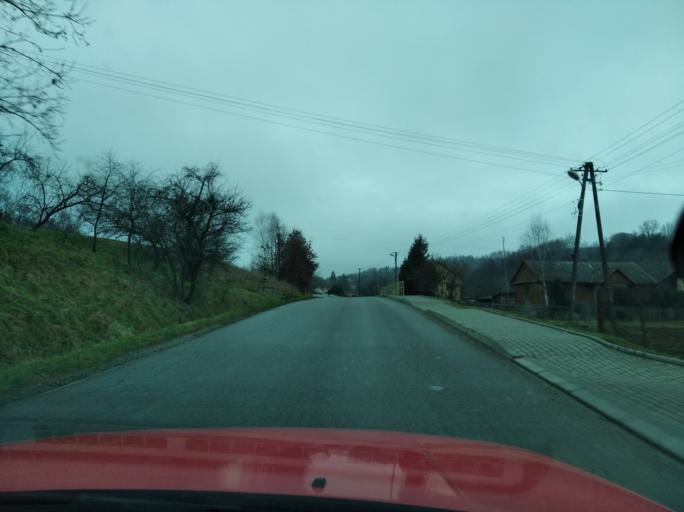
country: PL
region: Subcarpathian Voivodeship
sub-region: Powiat przemyski
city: Nienadowa
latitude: 49.8449
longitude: 22.4312
